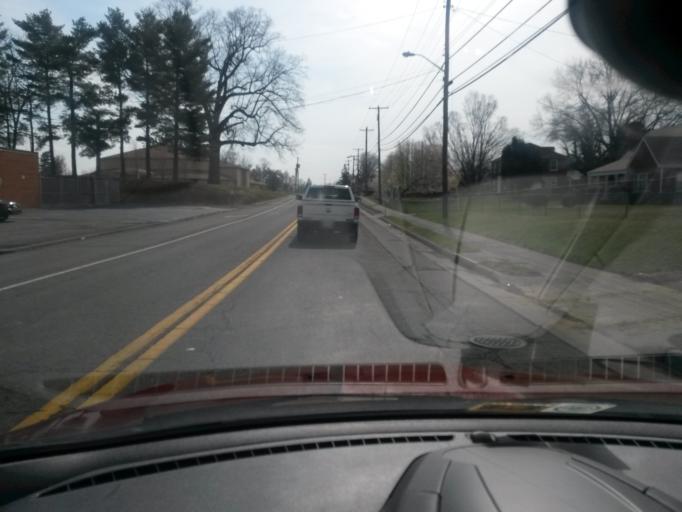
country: US
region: Virginia
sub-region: City of Roanoke
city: Roanoke
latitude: 37.3030
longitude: -79.9822
